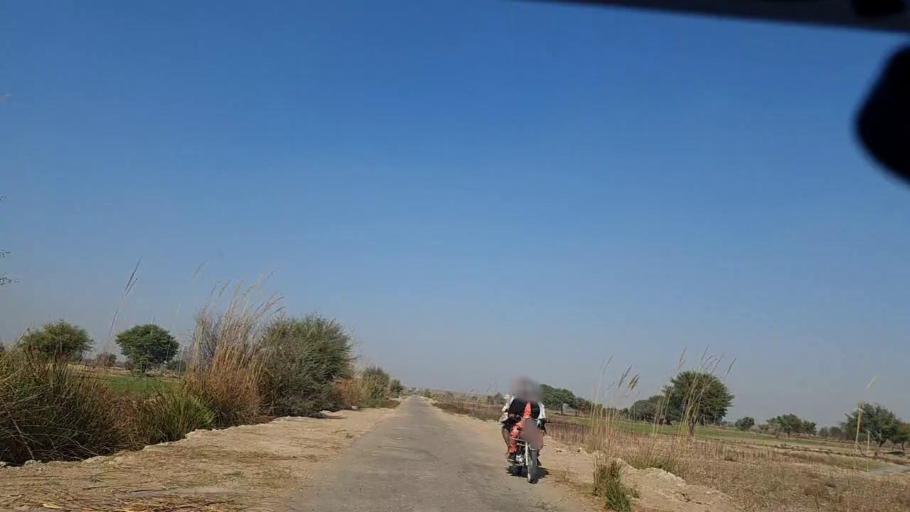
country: PK
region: Sindh
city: Khanpur
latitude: 27.5711
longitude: 69.3797
